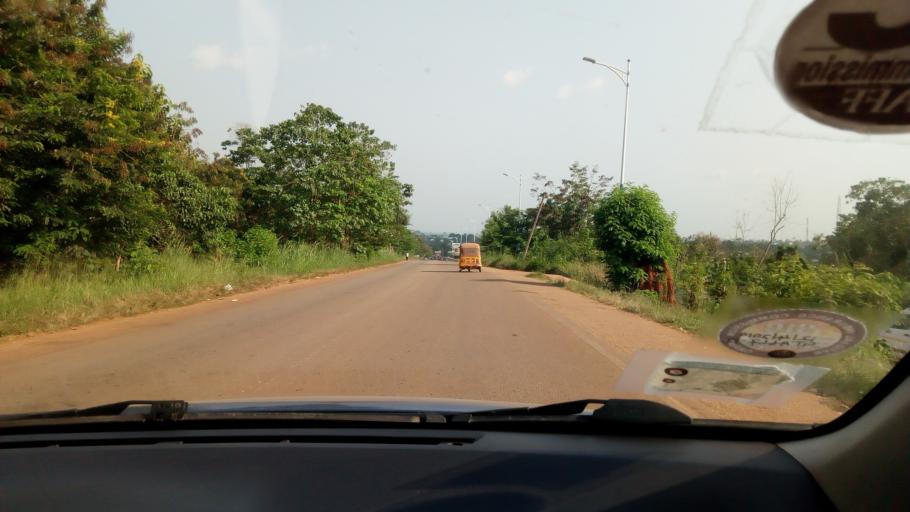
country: GH
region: Western
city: Bibiani
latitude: 6.8009
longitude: -2.5214
